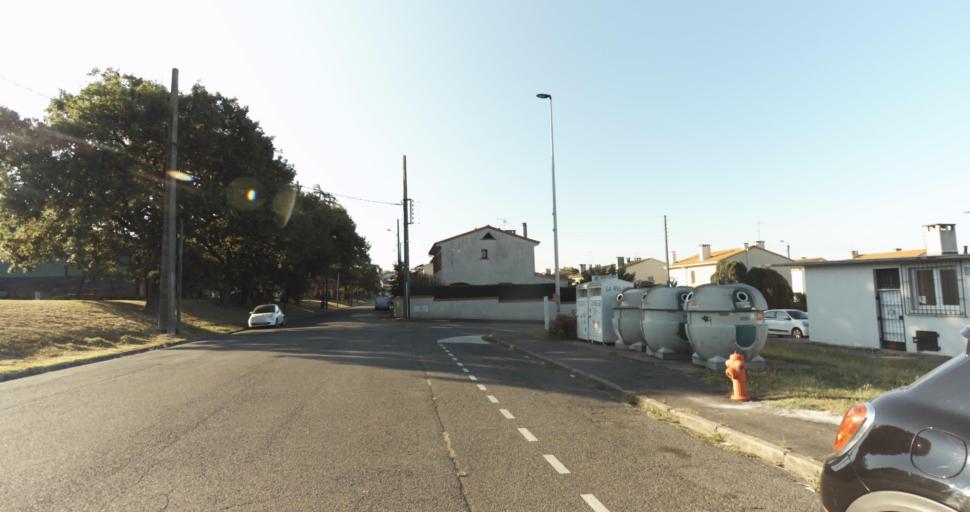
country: FR
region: Midi-Pyrenees
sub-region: Departement de la Haute-Garonne
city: L'Union
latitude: 43.6583
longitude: 1.4733
